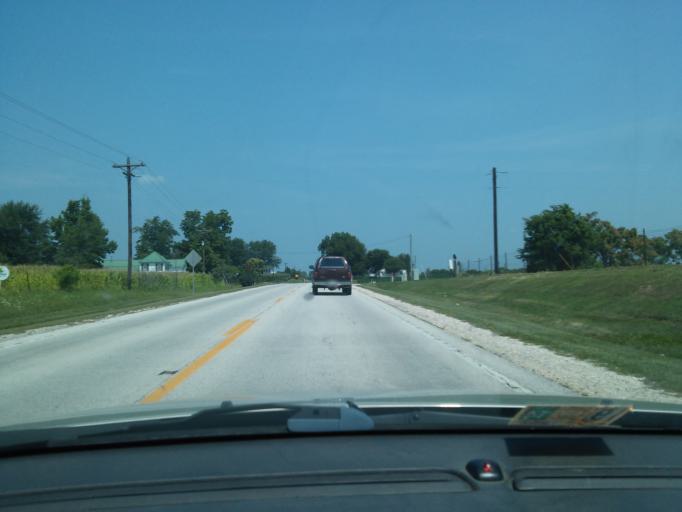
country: US
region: Illinois
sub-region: Pike County
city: Pittsfield
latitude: 39.5540
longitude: -90.9165
